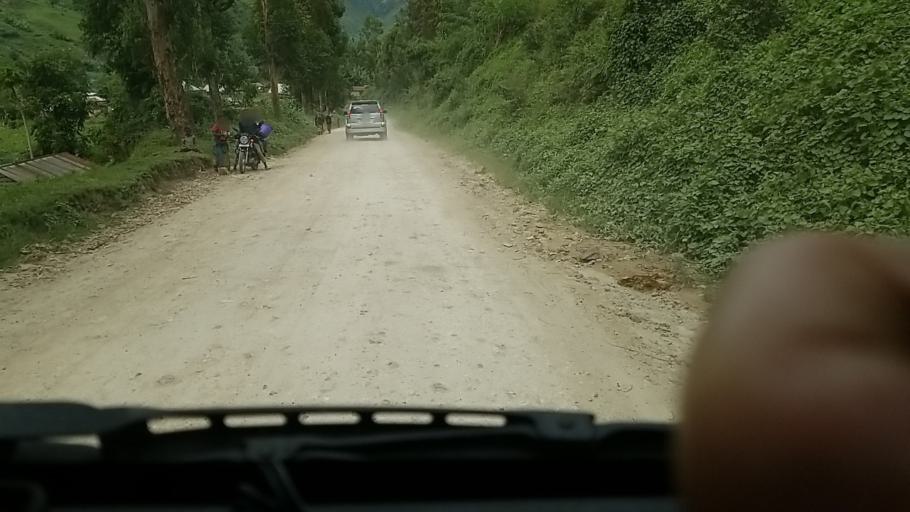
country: CD
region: Nord Kivu
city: Sake
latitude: -1.5907
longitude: 29.0421
